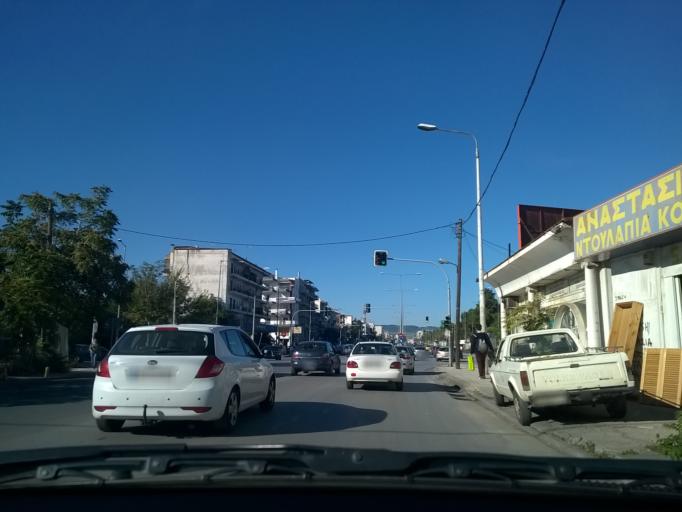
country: GR
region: Central Macedonia
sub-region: Nomos Thessalonikis
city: Ampelokipoi
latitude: 40.6563
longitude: 22.9345
